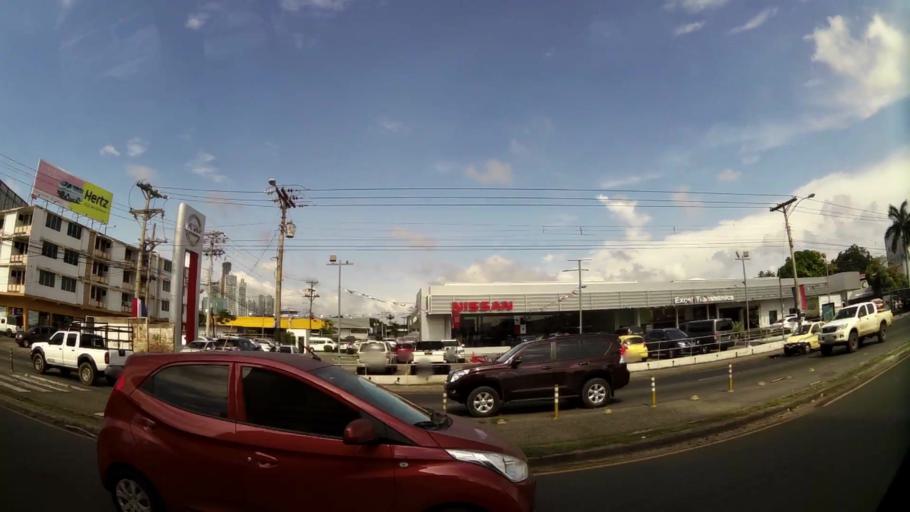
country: PA
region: Panama
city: Panama
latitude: 9.0019
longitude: -79.5234
